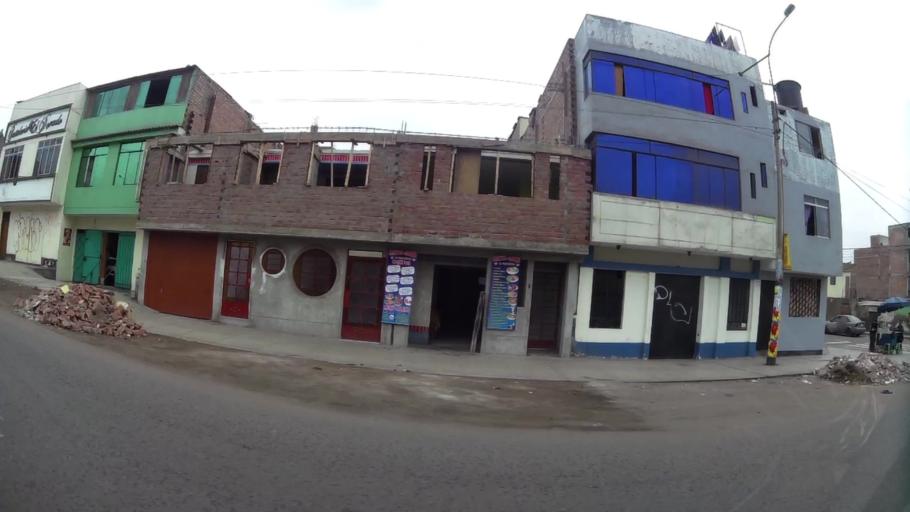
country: PE
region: Lima
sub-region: Lima
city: Surco
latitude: -12.1941
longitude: -76.9824
